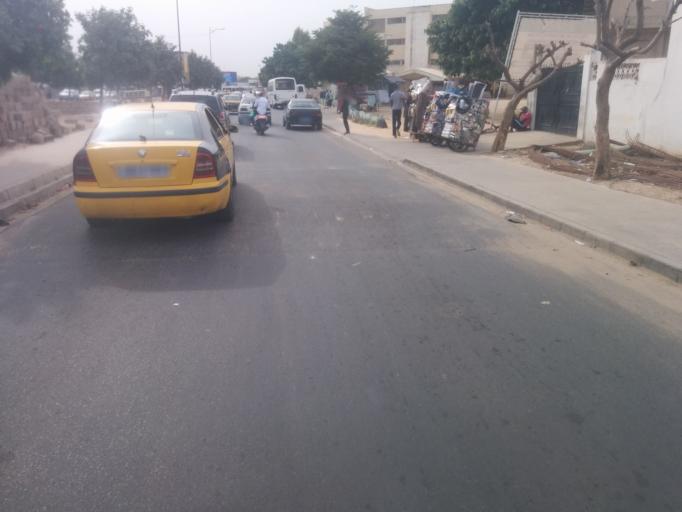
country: SN
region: Dakar
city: Grand Dakar
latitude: 14.7303
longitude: -17.4586
